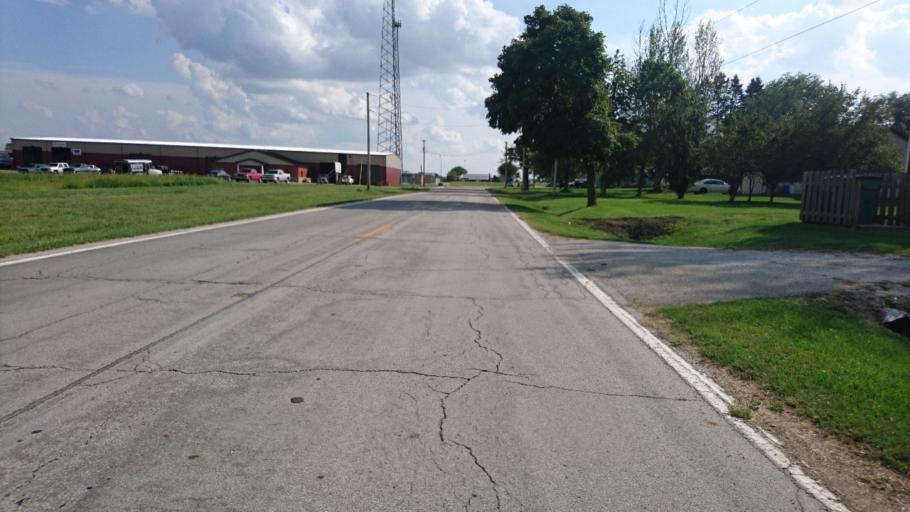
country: US
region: Illinois
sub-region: Logan County
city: Atlanta
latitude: 40.3151
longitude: -89.1659
